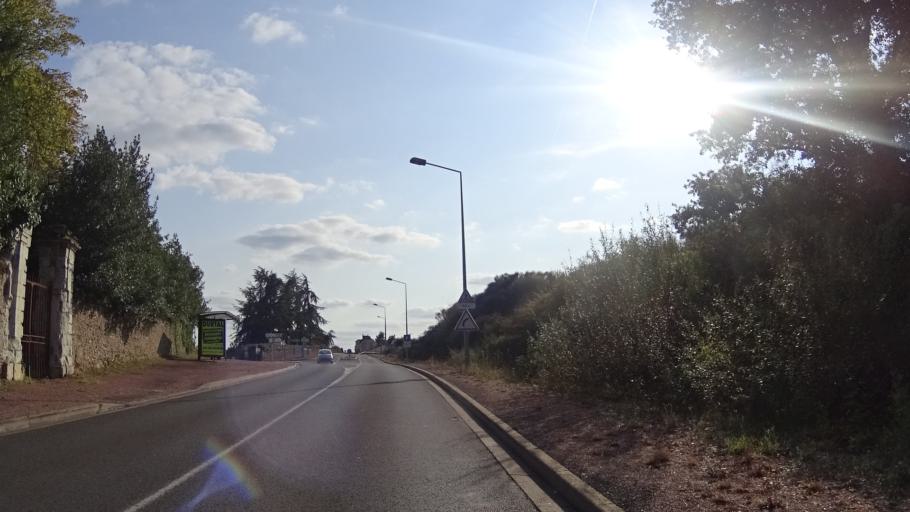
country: FR
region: Pays de la Loire
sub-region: Departement de Maine-et-Loire
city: Bouchemaine
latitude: 47.4107
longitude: -0.6196
